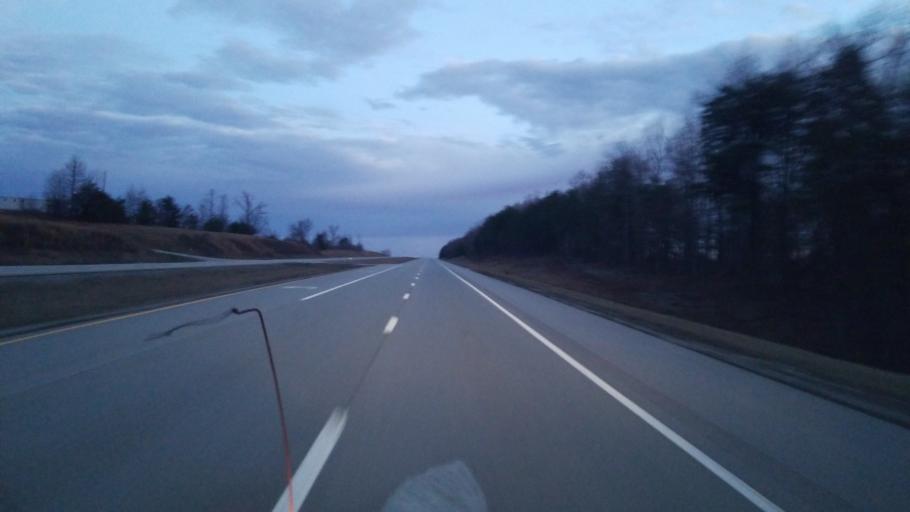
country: US
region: Tennessee
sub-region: Van Buren County
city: Spencer
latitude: 35.6525
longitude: -85.4738
